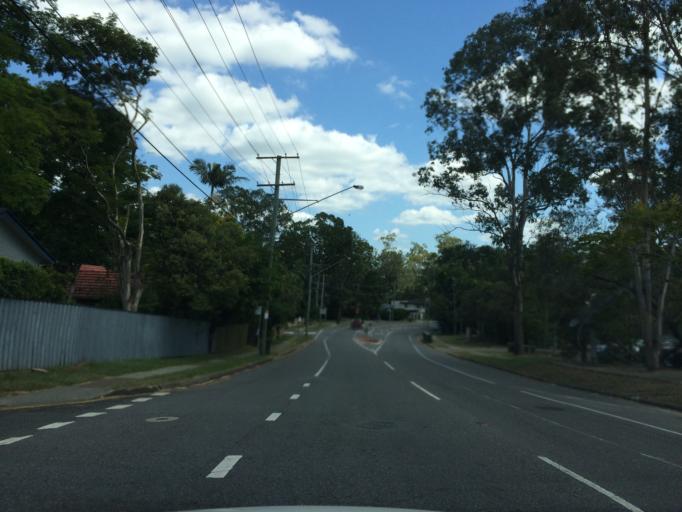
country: AU
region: Queensland
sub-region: Brisbane
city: Kenmore Hills
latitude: -27.5066
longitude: 152.9353
